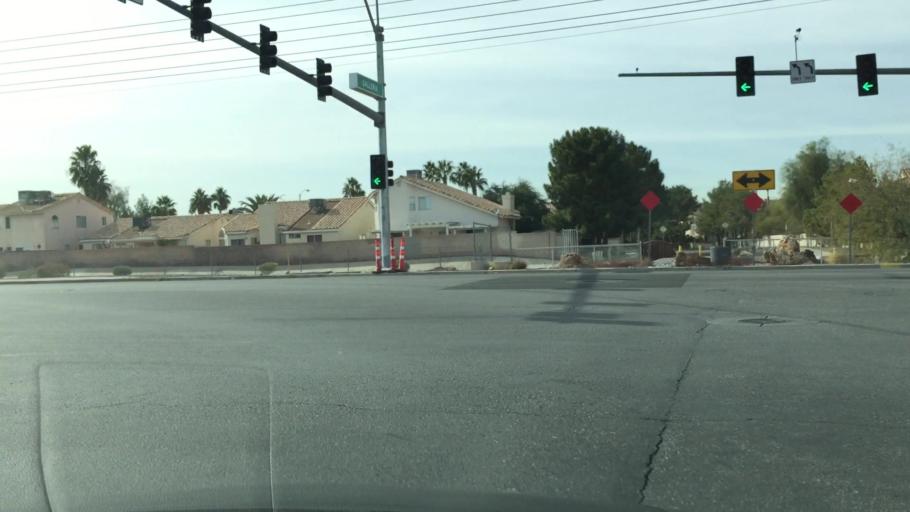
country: US
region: Nevada
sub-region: Clark County
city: Whitney
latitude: 36.0709
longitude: -115.0460
